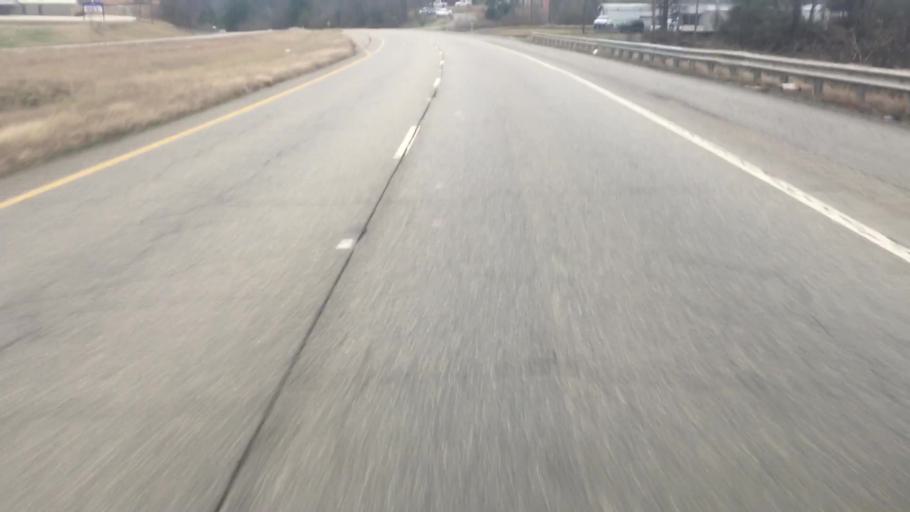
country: US
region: Alabama
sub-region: Walker County
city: Dora
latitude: 33.7960
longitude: -87.1097
